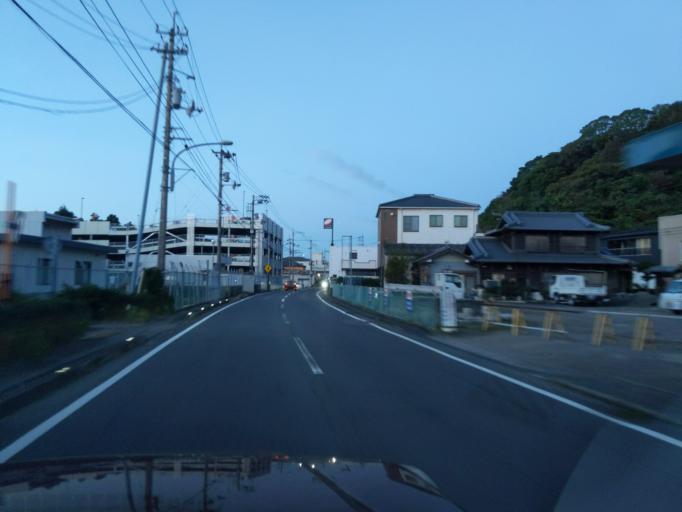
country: JP
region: Tokushima
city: Anan
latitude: 33.8789
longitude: 134.6506
